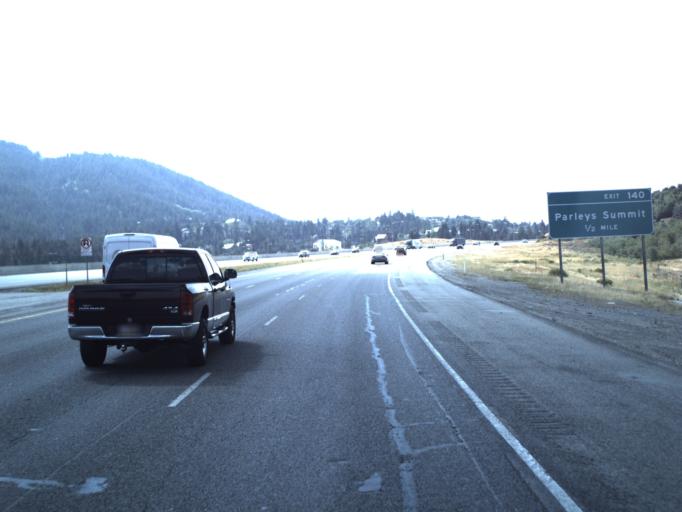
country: US
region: Utah
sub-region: Summit County
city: Summit Park
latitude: 40.7503
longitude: -111.6016
